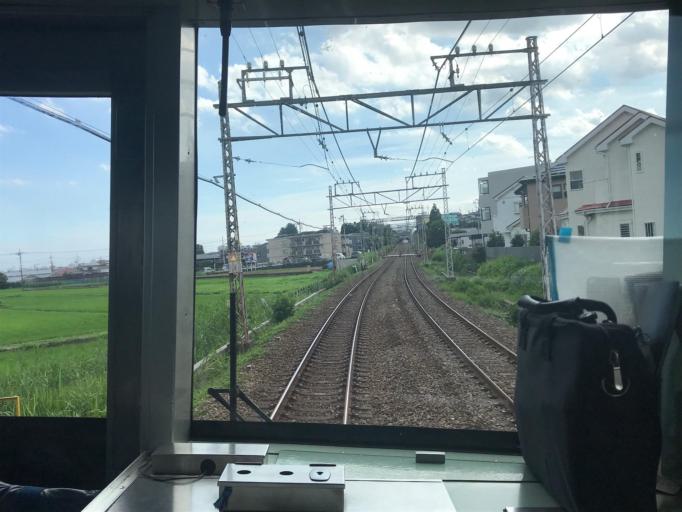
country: JP
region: Kanagawa
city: Atsugi
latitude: 35.4231
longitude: 139.3506
